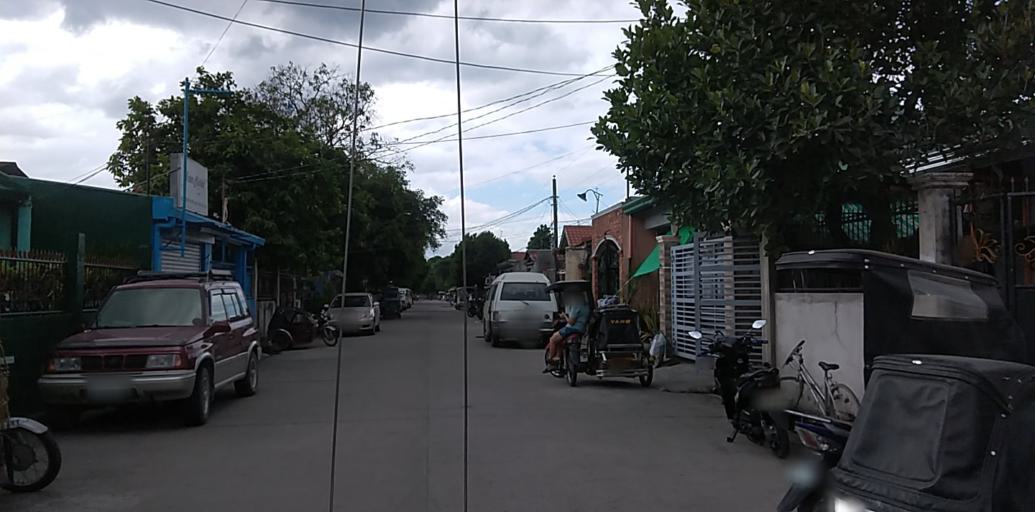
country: PH
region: Central Luzon
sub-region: Province of Pampanga
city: Pio
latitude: 15.0461
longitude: 120.5277
